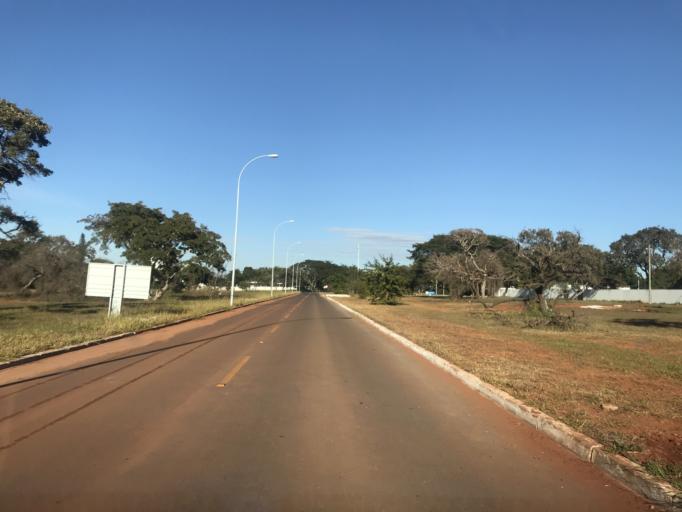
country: BR
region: Federal District
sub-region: Brasilia
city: Brasilia
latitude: -15.8275
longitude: -47.8946
